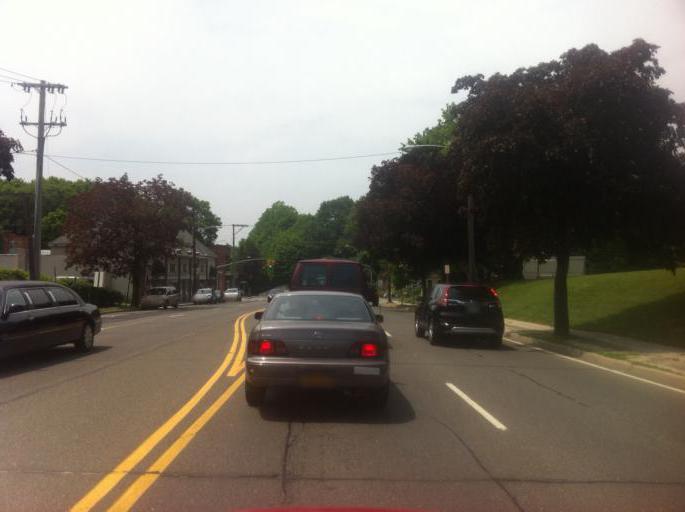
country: US
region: New York
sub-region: Nassau County
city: Glen Cove
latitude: 40.8706
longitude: -73.6278
